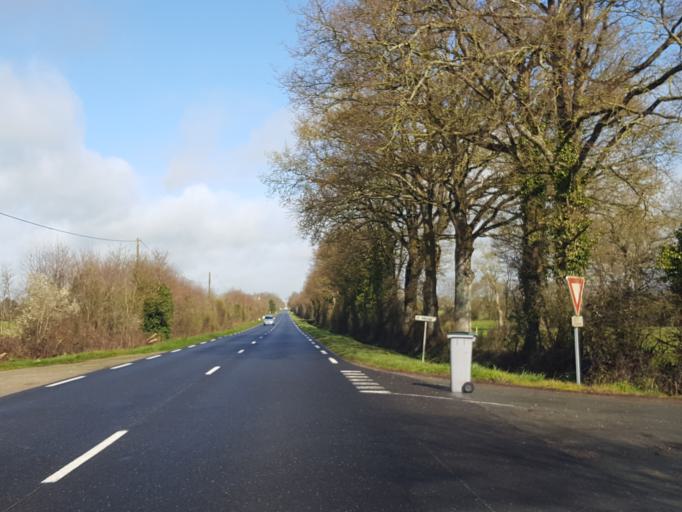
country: FR
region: Pays de la Loire
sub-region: Departement de la Vendee
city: Les Lucs-sur-Boulogne
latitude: 46.8212
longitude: -1.4709
